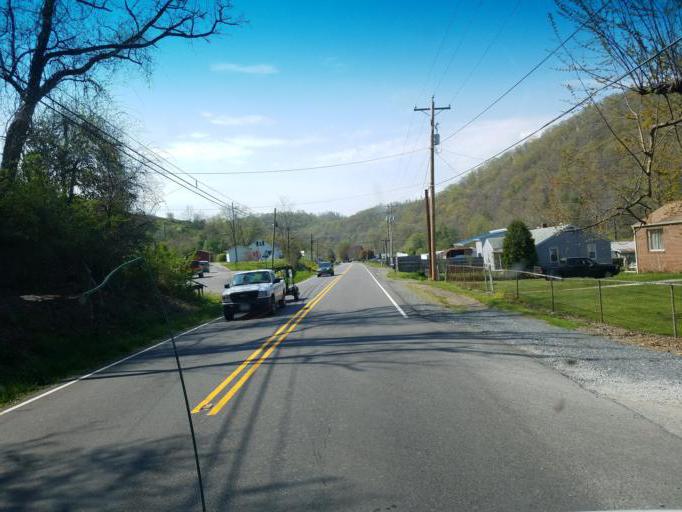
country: US
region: Virginia
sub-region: Smyth County
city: Marion
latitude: 36.8182
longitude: -81.4696
